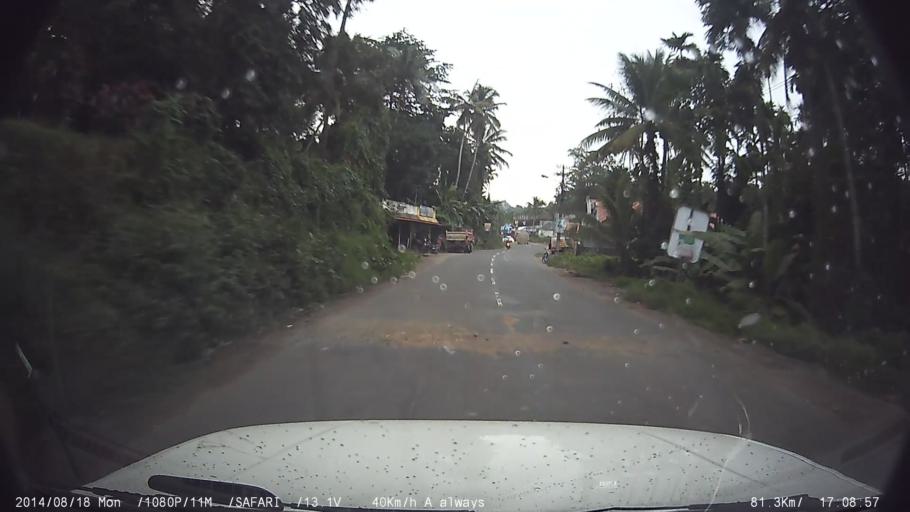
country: IN
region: Kerala
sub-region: Ernakulam
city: Piravam
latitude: 9.8671
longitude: 76.5969
